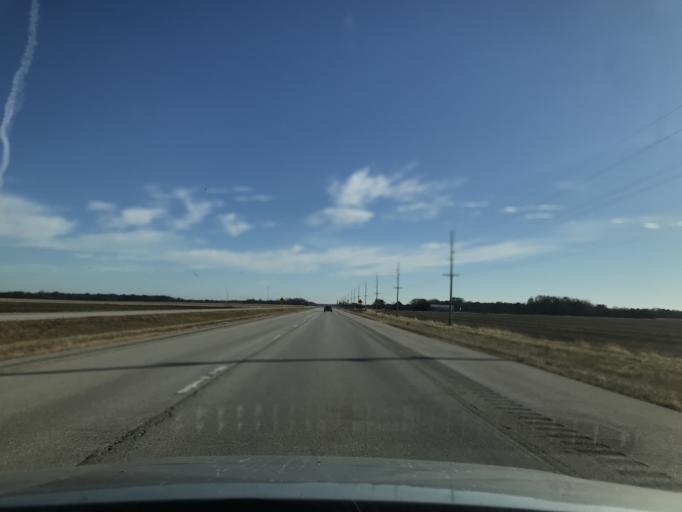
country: US
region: Illinois
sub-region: Hancock County
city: Carthage
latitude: 40.4152
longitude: -91.0589
